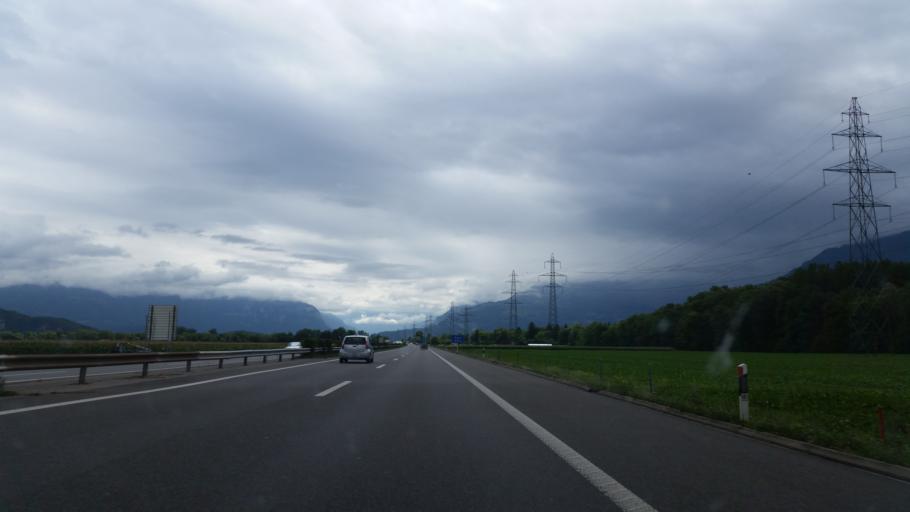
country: CH
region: Vaud
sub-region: Aigle District
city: Aigle
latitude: 46.3328
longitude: 6.9336
